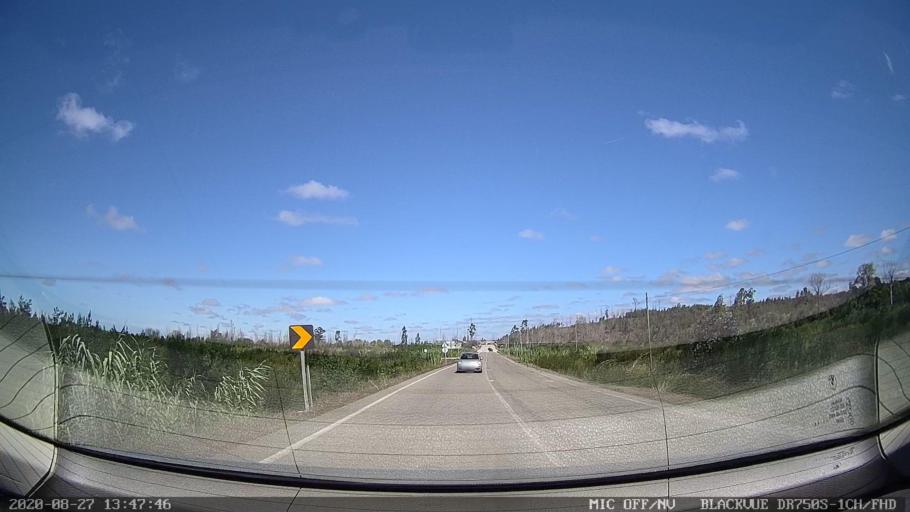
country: PT
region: Coimbra
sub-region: Mira
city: Mira
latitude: 40.3849
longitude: -8.7432
